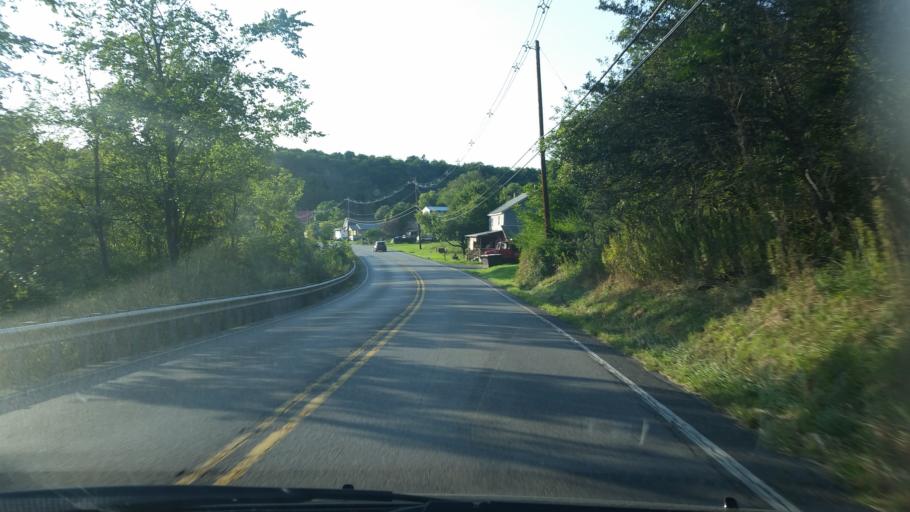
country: US
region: Pennsylvania
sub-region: Blair County
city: Greenwood
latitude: 40.5690
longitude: -78.3441
